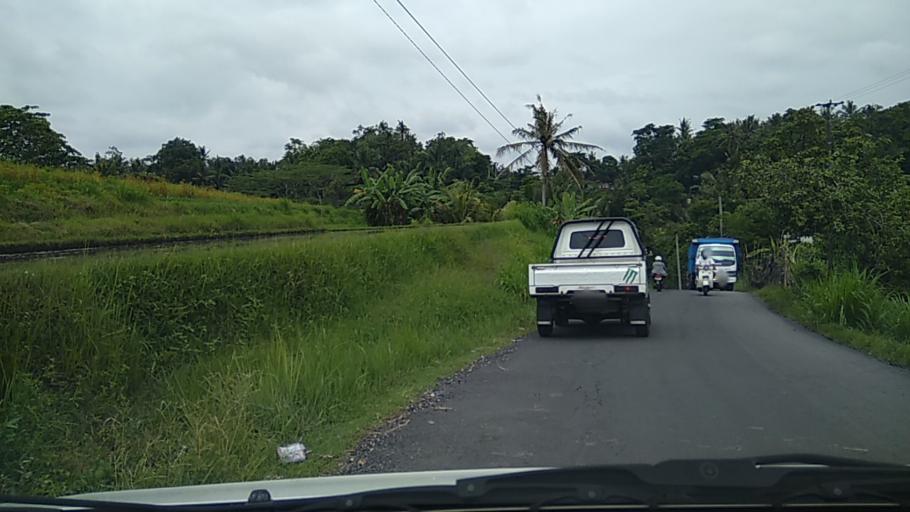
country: ID
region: Bali
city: Banjar Keraman
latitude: -8.5234
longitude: 115.2208
